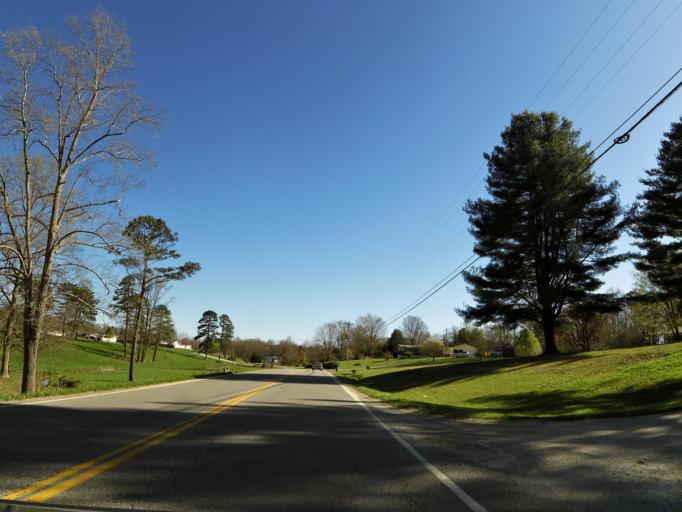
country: US
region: Tennessee
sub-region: Scott County
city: Huntsville
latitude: 36.4257
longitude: -84.4411
